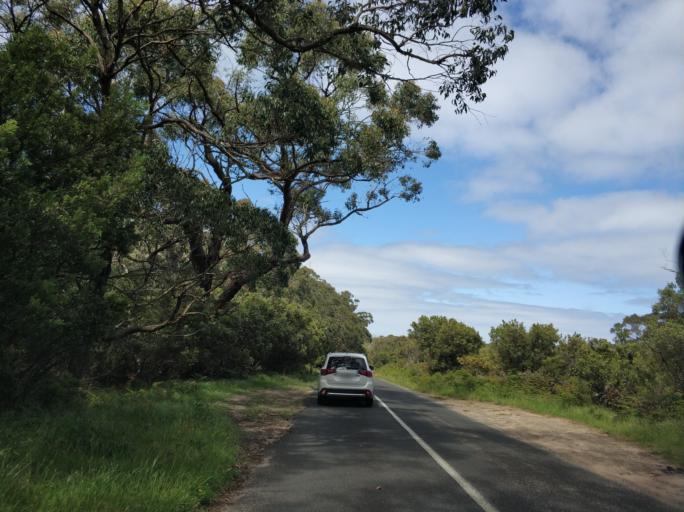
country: AU
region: Victoria
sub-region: Colac-Otway
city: Apollo Bay
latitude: -38.8437
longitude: 143.5336
